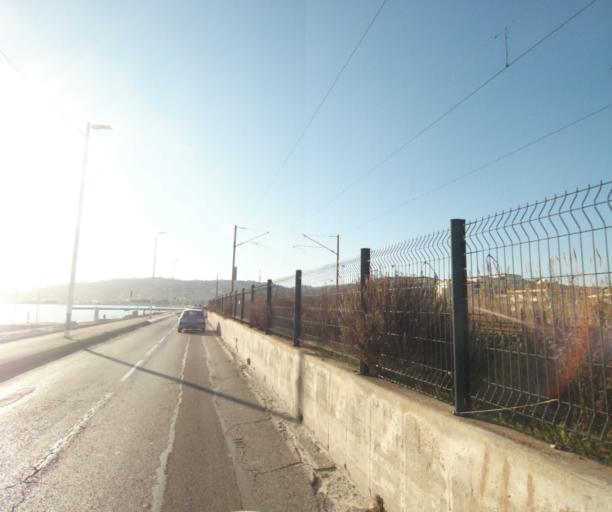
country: FR
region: Provence-Alpes-Cote d'Azur
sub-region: Departement des Alpes-Maritimes
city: Antibes
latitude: 43.5710
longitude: 7.0942
